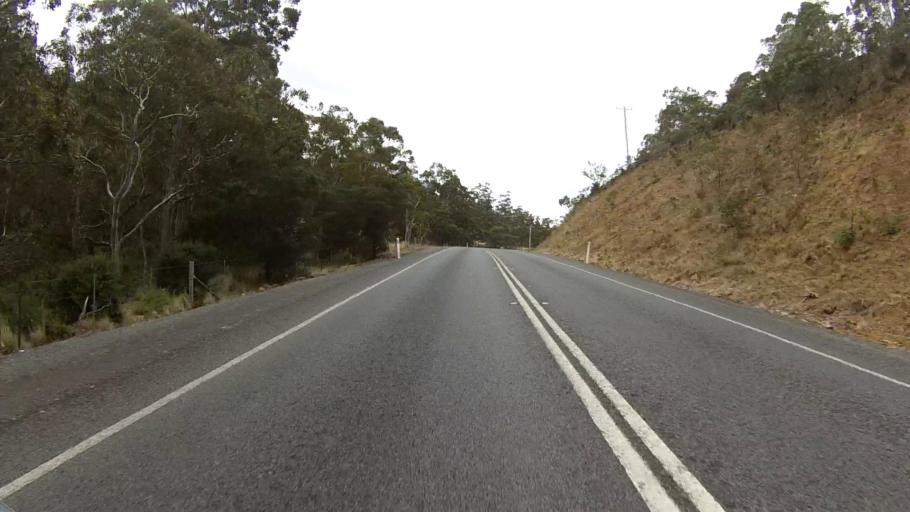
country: AU
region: Tasmania
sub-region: Sorell
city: Sorell
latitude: -42.6675
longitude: 147.5280
